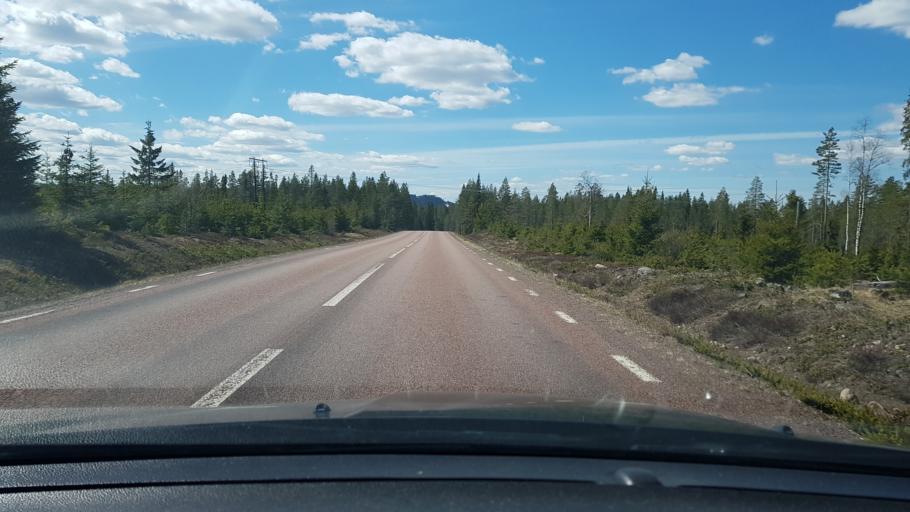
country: SE
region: Dalarna
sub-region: Malung-Saelens kommun
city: Malung
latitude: 61.0533
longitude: 13.4249
